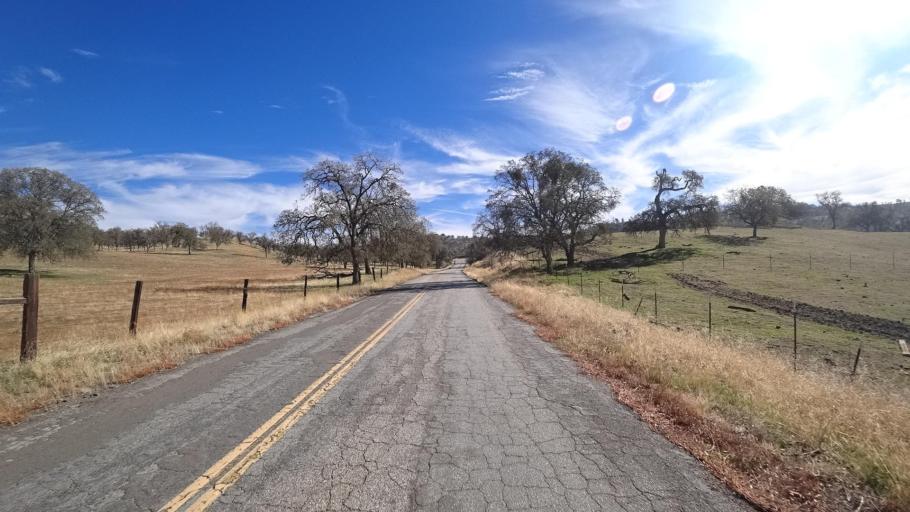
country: US
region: California
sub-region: Kern County
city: Alta Sierra
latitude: 35.6301
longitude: -118.7910
